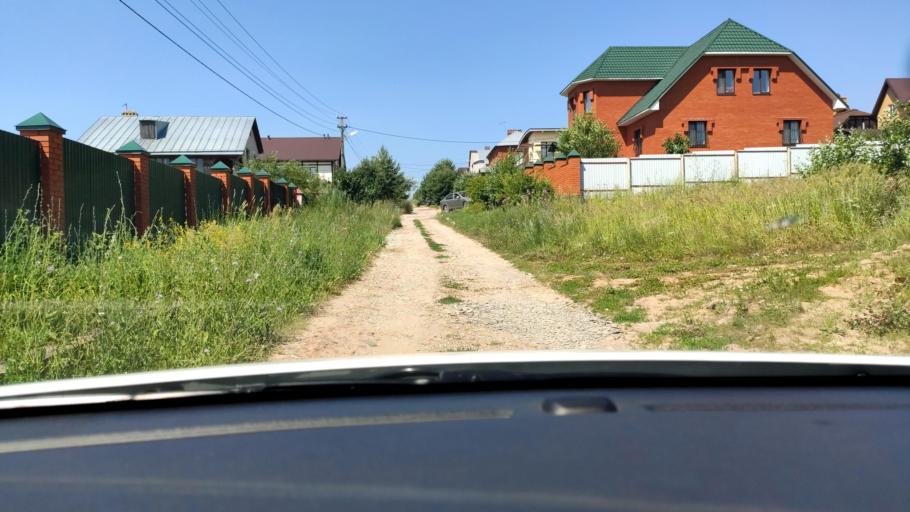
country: RU
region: Tatarstan
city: Stolbishchi
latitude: 55.7533
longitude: 49.2934
